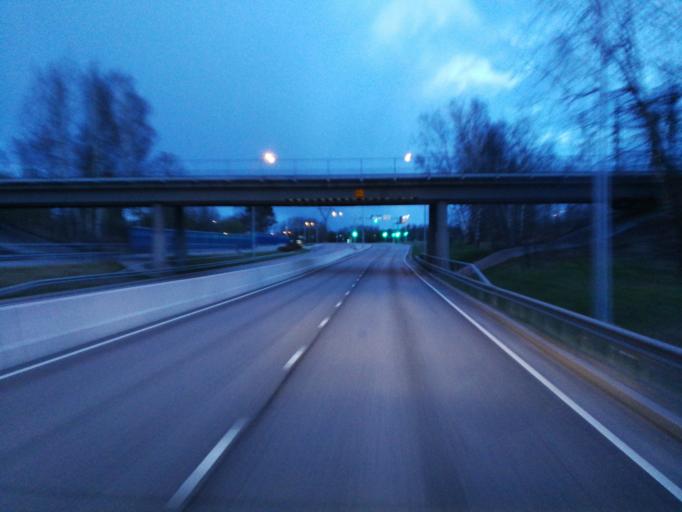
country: FI
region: Varsinais-Suomi
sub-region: Turku
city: Raisio
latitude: 60.4586
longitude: 22.1951
